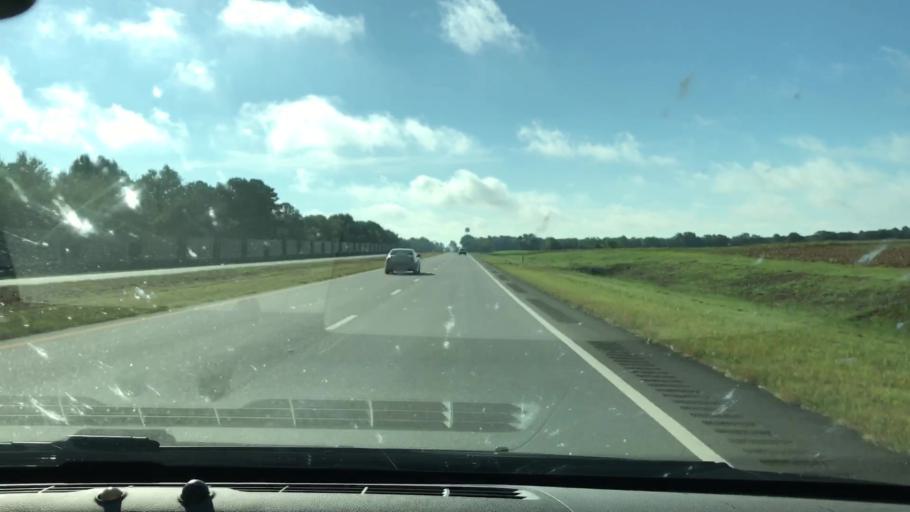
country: US
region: Georgia
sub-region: Terrell County
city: Dawson
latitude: 31.7287
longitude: -84.3619
